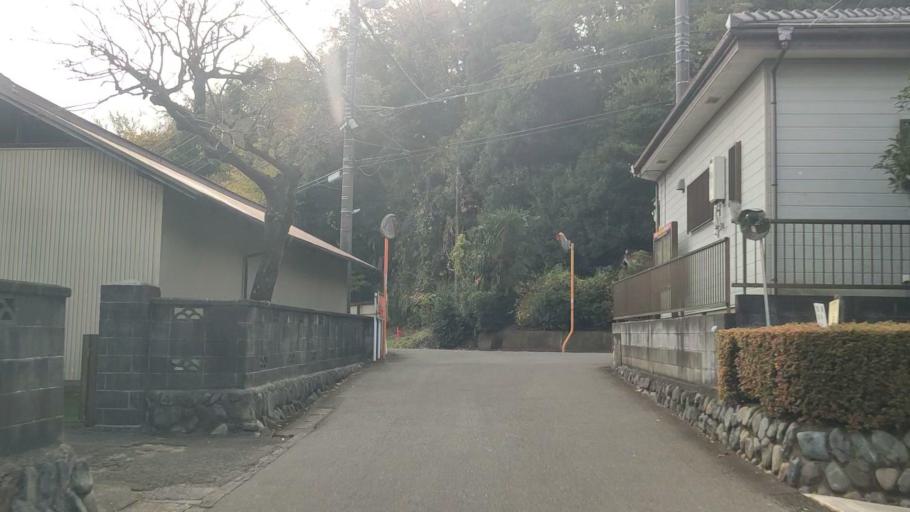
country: JP
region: Kanagawa
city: Minami-rinkan
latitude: 35.4823
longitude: 139.4684
